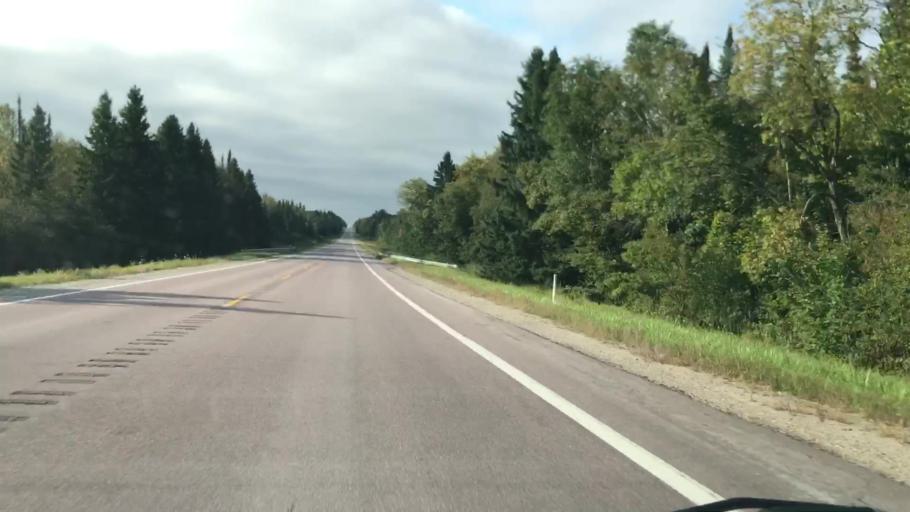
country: US
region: Michigan
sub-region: Luce County
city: Newberry
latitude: 46.3008
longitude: -85.5684
